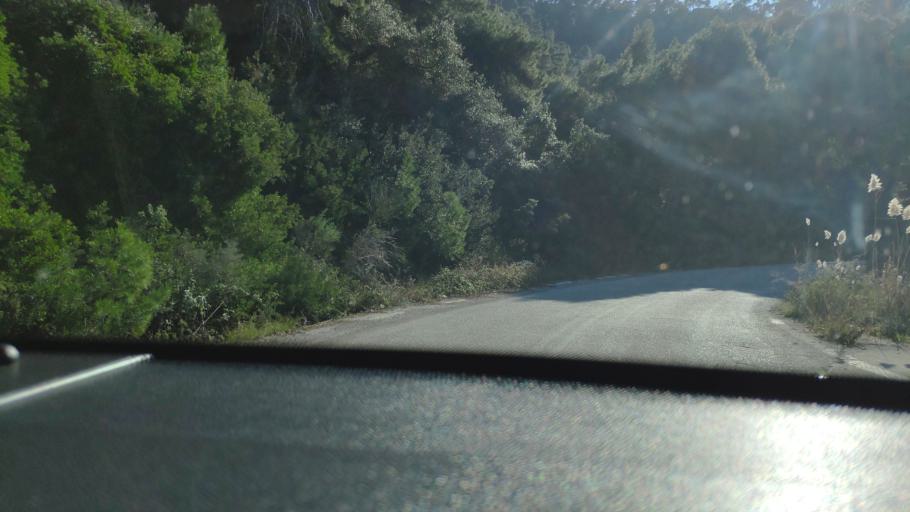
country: GR
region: Peloponnese
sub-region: Nomos Korinthias
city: Agioi Theodoroi
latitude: 38.0592
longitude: 23.1066
